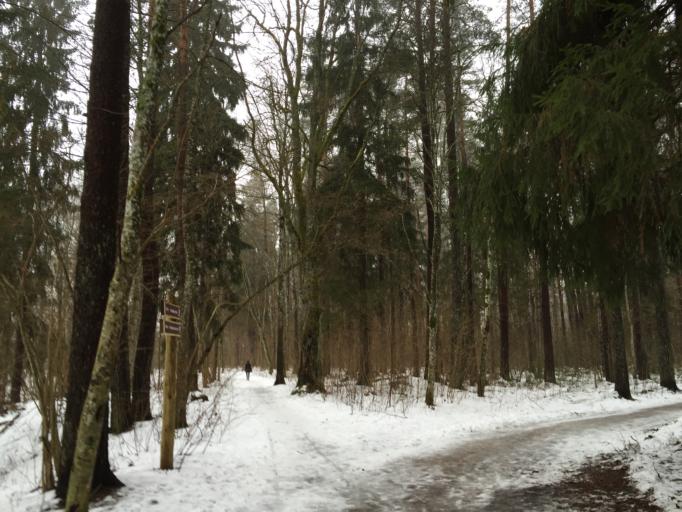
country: LV
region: Sigulda
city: Sigulda
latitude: 57.1711
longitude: 24.8645
